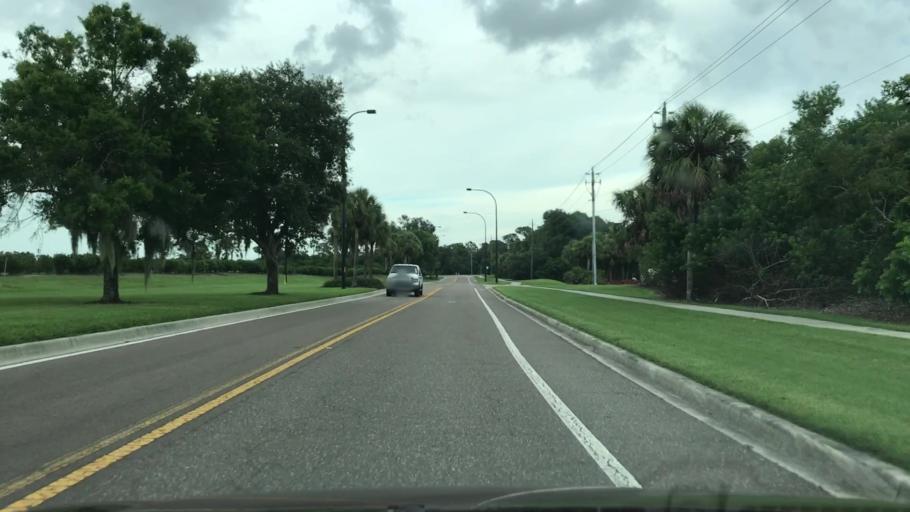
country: US
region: Florida
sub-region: Sarasota County
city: Vamo
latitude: 27.2379
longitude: -82.4790
